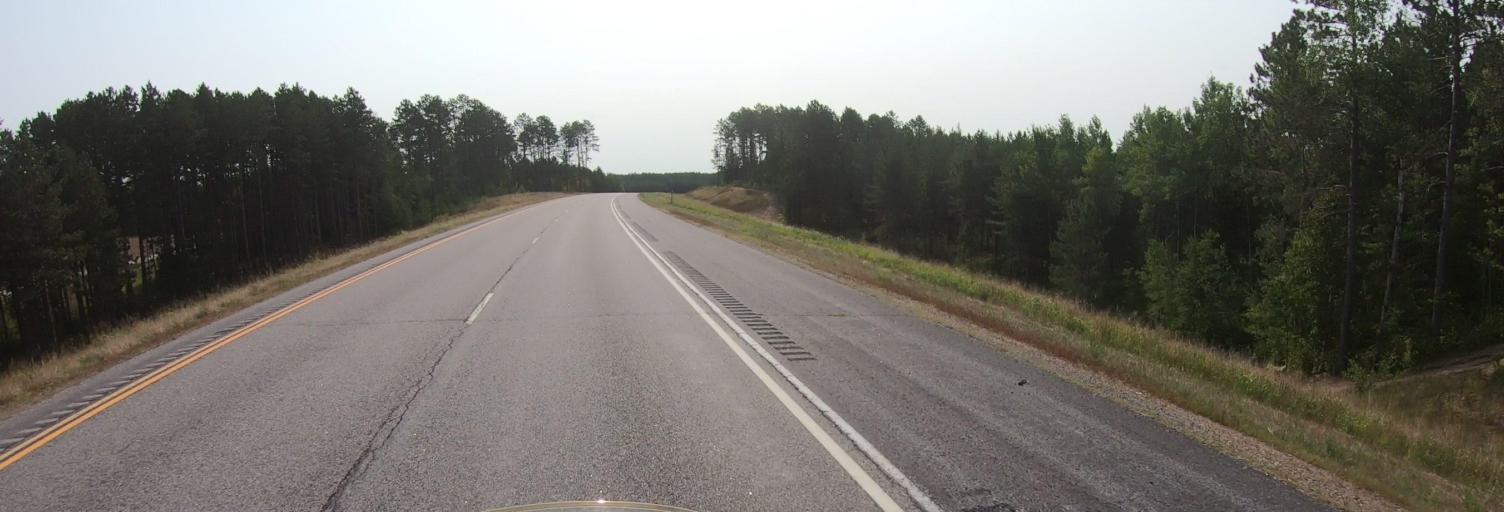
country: US
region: Minnesota
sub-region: Saint Louis County
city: Parkville
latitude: 47.6613
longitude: -92.5867
